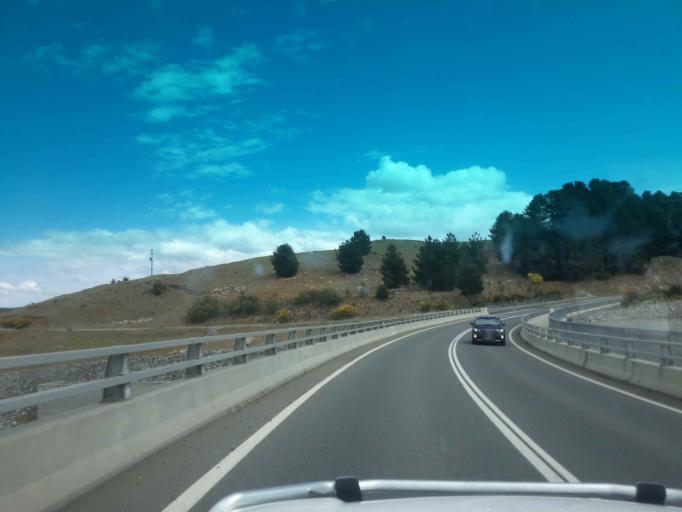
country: AU
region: New South Wales
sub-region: Snowy River
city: Jindabyne
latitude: -36.4352
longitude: 148.6311
